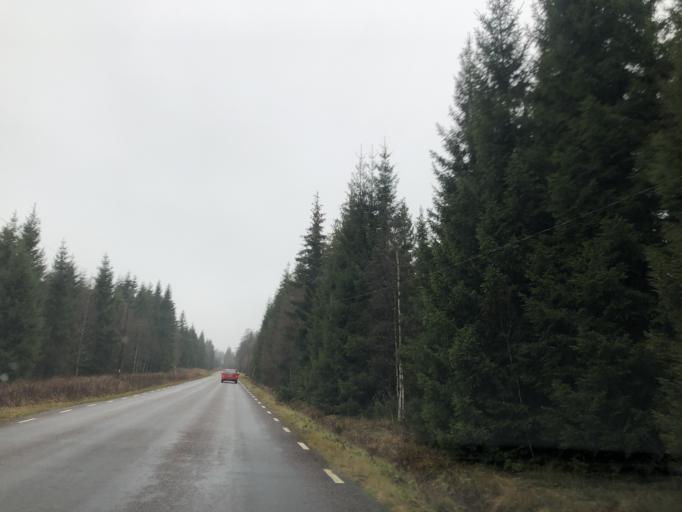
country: SE
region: Vaestra Goetaland
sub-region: Ulricehamns Kommun
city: Ulricehamn
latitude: 57.7480
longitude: 13.5270
